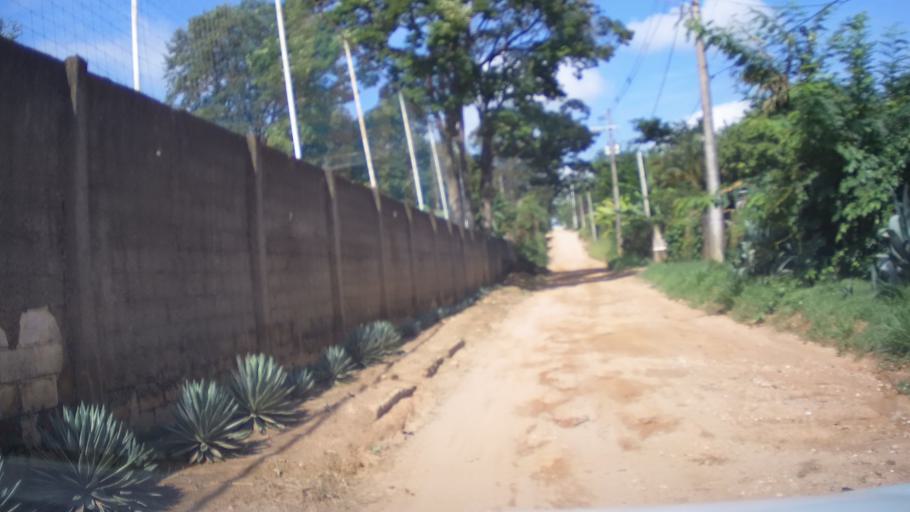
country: BR
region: Sao Paulo
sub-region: Itupeva
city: Itupeva
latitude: -23.2197
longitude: -47.0655
